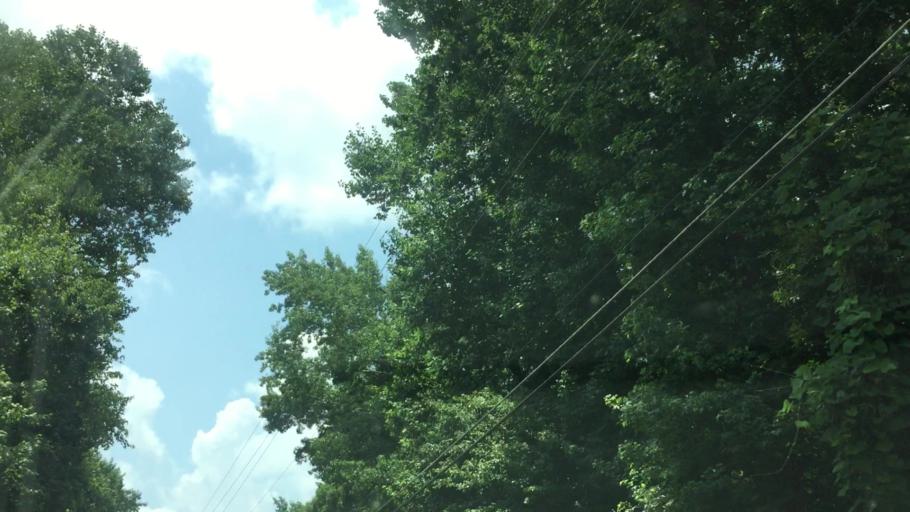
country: US
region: Georgia
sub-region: Carroll County
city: Carrollton
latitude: 33.6153
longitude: -84.9919
